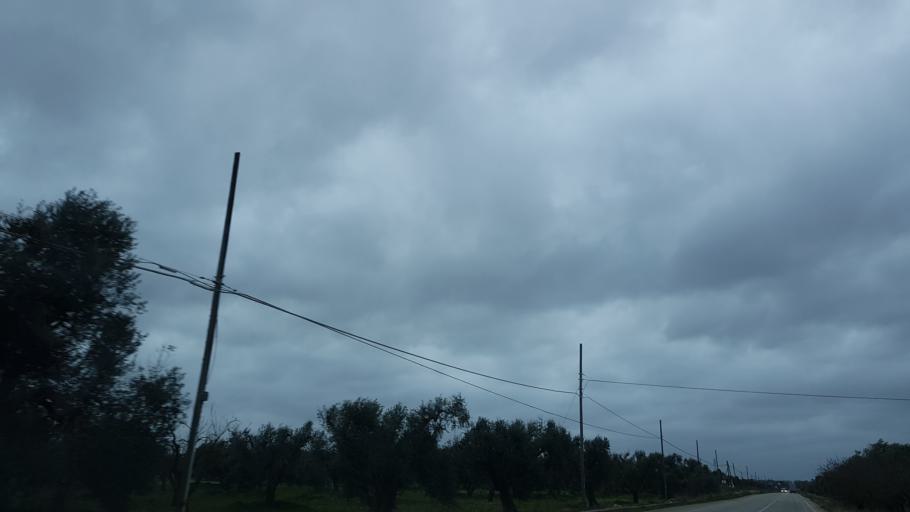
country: IT
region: Apulia
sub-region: Provincia di Brindisi
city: San Vito dei Normanni
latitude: 40.6525
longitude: 17.7991
